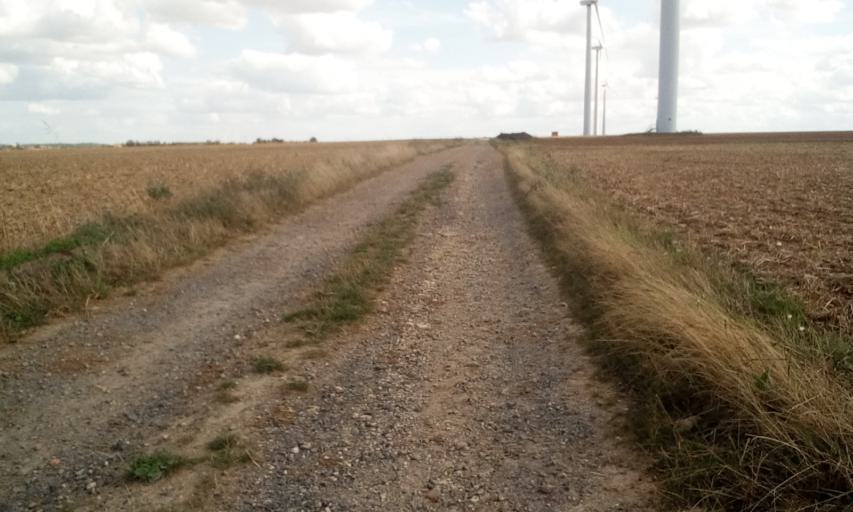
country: FR
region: Lower Normandy
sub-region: Departement du Calvados
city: Bellengreville
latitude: 49.1035
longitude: -0.2349
